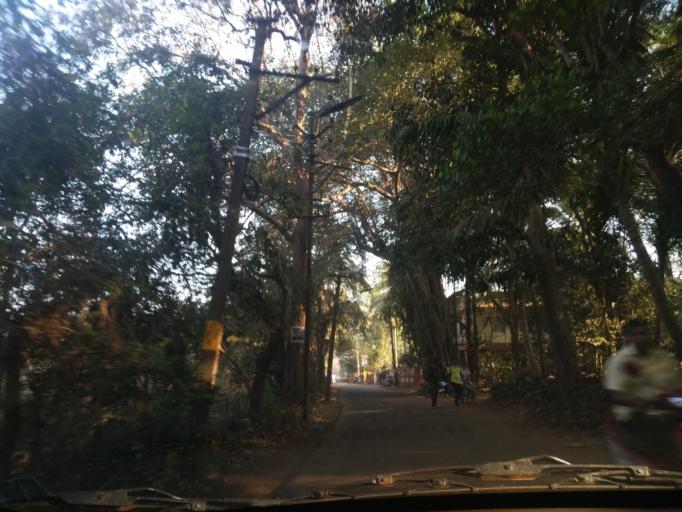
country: IN
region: Goa
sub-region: South Goa
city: Davorlim
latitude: 15.2800
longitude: 74.0062
